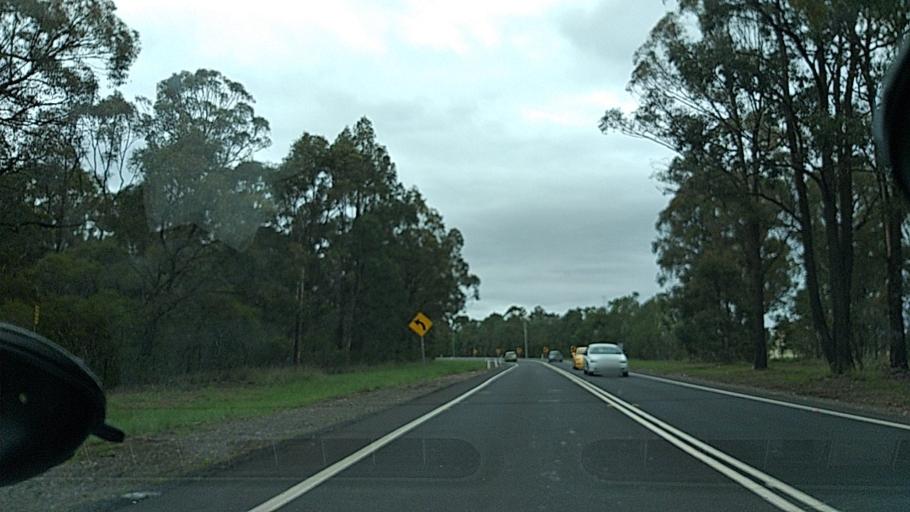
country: AU
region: New South Wales
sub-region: Penrith Municipality
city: Werrington Downs
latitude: -33.7078
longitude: 150.7230
